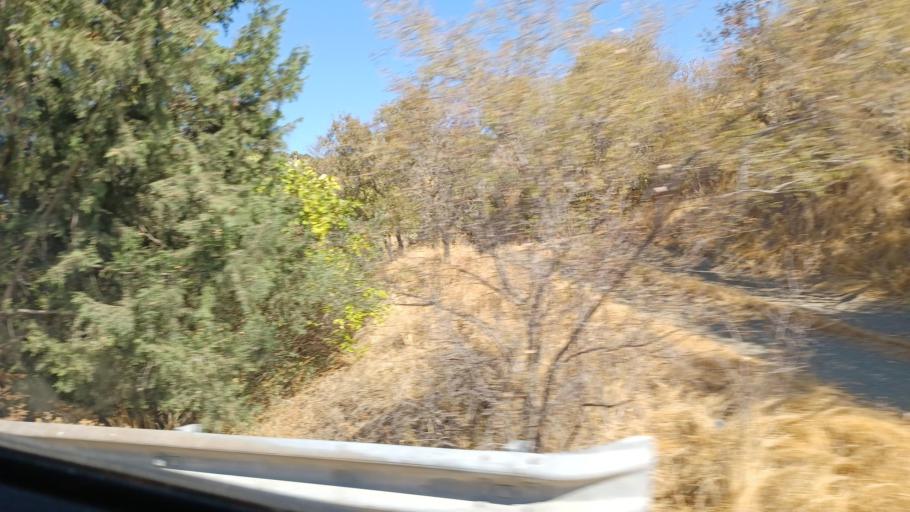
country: CY
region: Pafos
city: Mesogi
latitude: 34.9221
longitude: 32.5766
